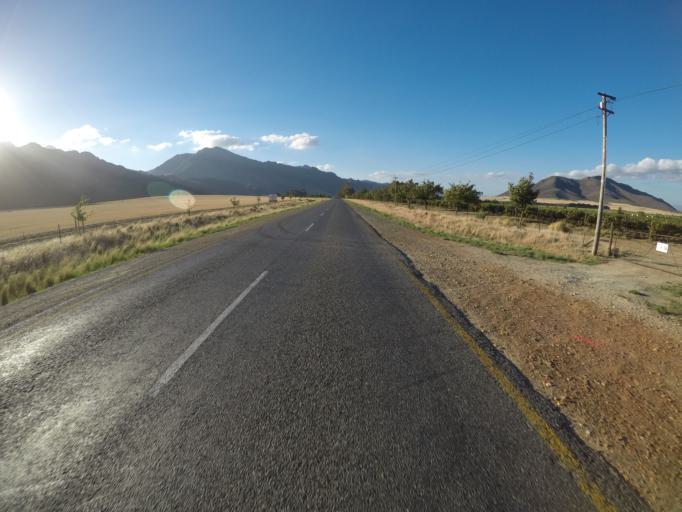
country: ZA
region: Western Cape
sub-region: Cape Winelands District Municipality
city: Worcester
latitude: -33.8929
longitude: 19.3663
